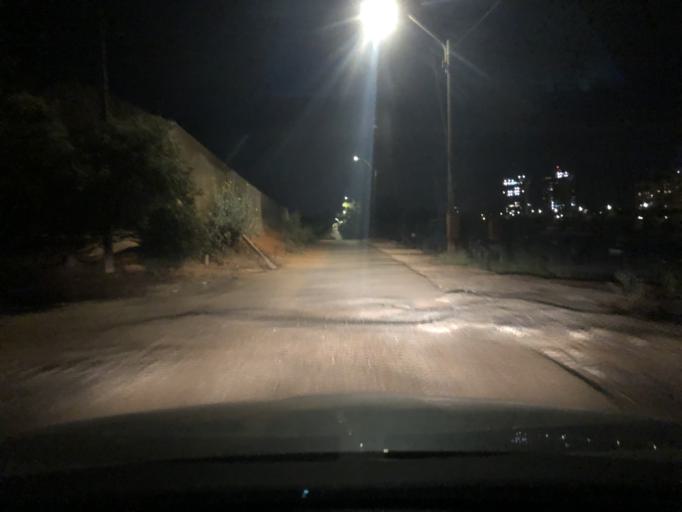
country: IL
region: Central District
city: Hod HaSharon
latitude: 32.1638
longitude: 34.8962
